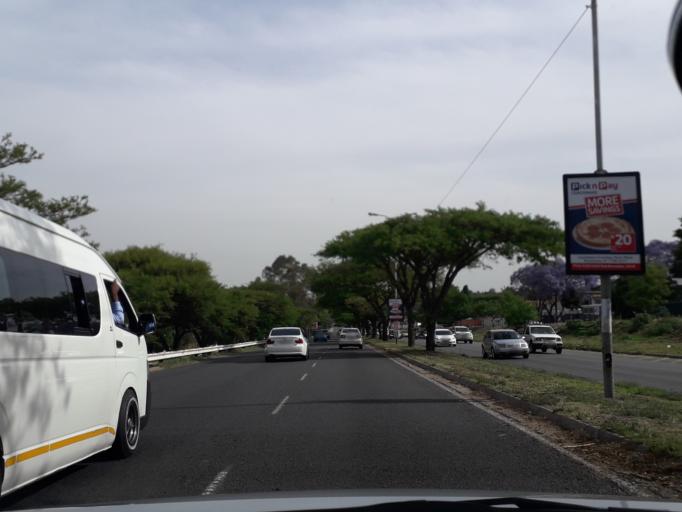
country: ZA
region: Gauteng
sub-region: City of Johannesburg Metropolitan Municipality
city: Johannesburg
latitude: -26.0776
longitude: 28.0260
